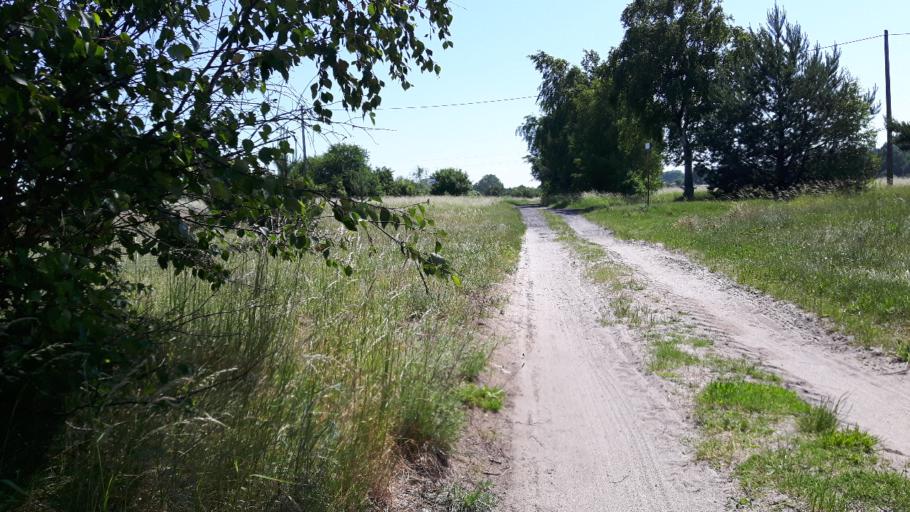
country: PL
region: Pomeranian Voivodeship
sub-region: Powiat slupski
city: Smoldzino
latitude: 54.6673
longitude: 17.2042
